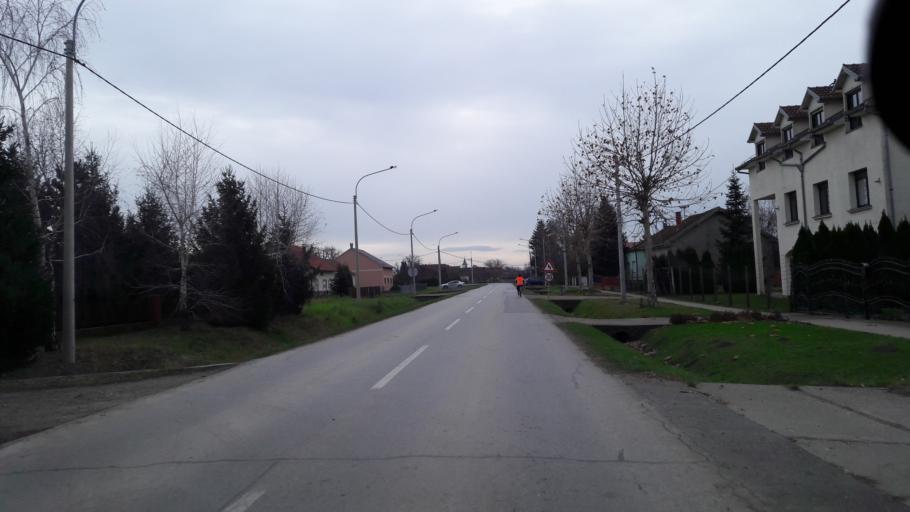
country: HR
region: Osjecko-Baranjska
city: Vladislavci
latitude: 45.4656
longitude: 18.5681
